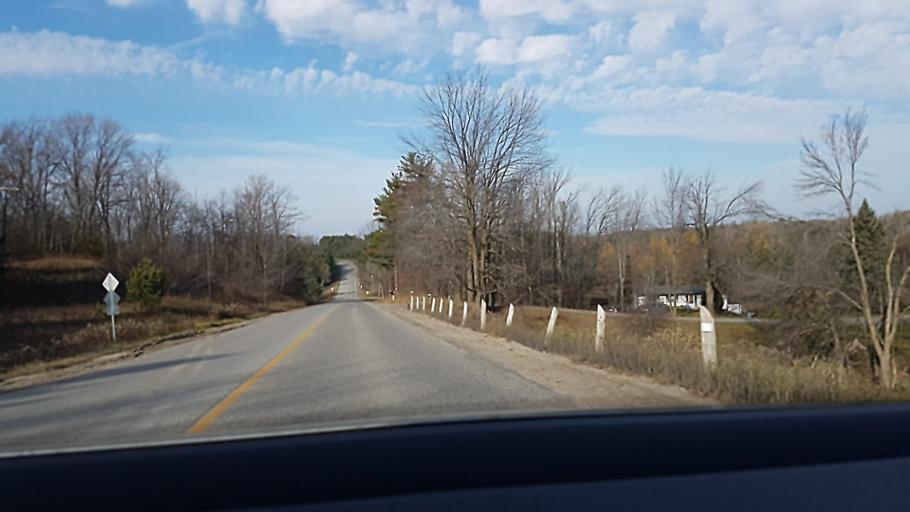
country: CA
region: Ontario
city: Bradford West Gwillimbury
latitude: 44.0556
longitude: -79.7751
